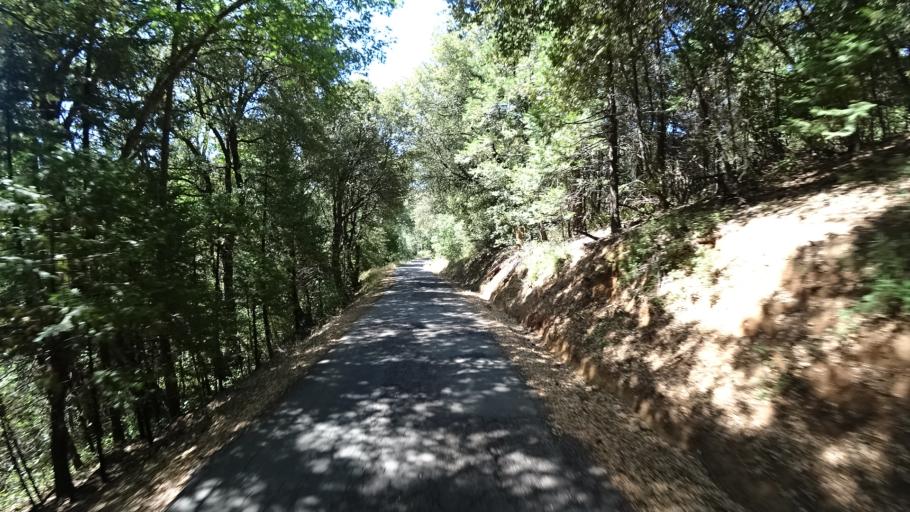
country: US
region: California
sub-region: Amador County
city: Pioneer
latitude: 38.3913
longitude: -120.5013
